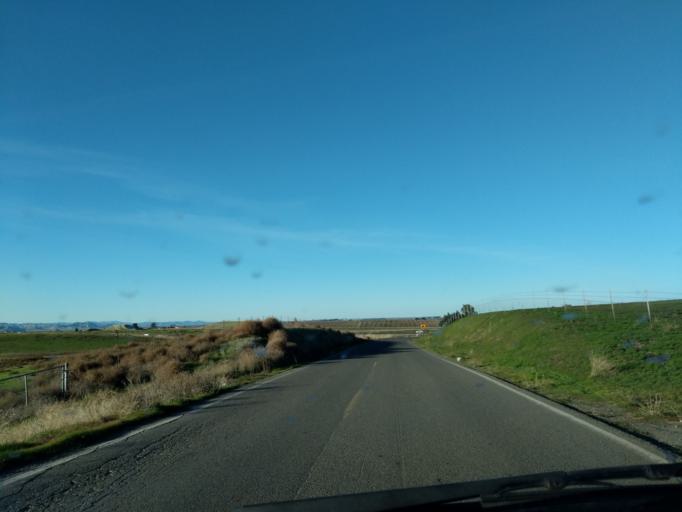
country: US
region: California
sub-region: Merced County
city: Los Banos
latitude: 37.0534
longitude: -120.9545
